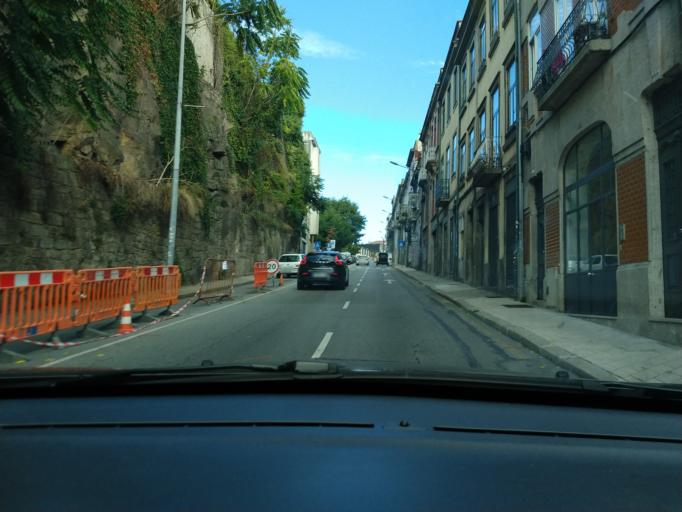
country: PT
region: Porto
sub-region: Porto
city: Porto
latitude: 41.1539
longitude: -8.6025
